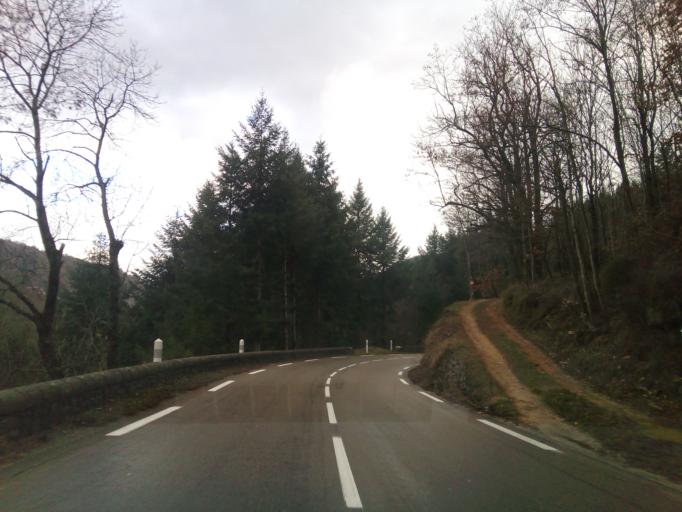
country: FR
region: Rhone-Alpes
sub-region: Departement de l'Ardeche
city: Le Cheylard
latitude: 44.8985
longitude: 4.4854
